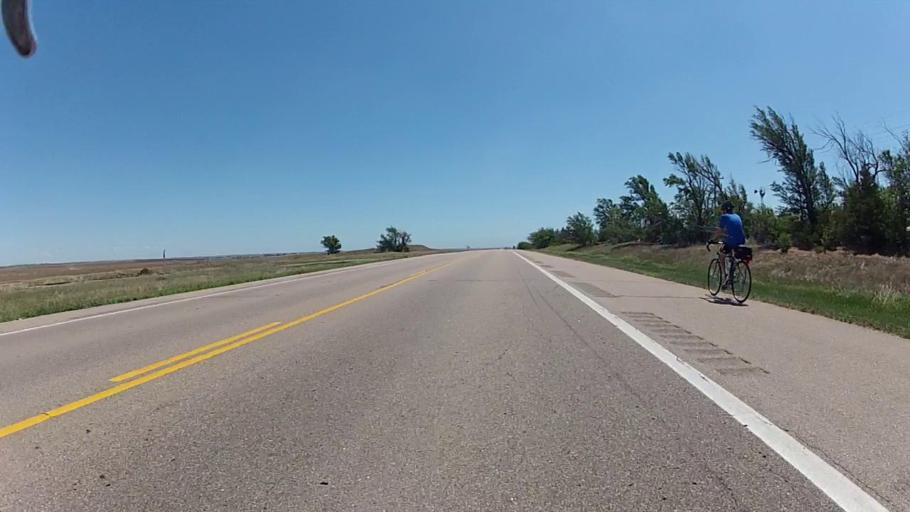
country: US
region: Kansas
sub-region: Ford County
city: Dodge City
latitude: 37.7074
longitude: -100.1290
